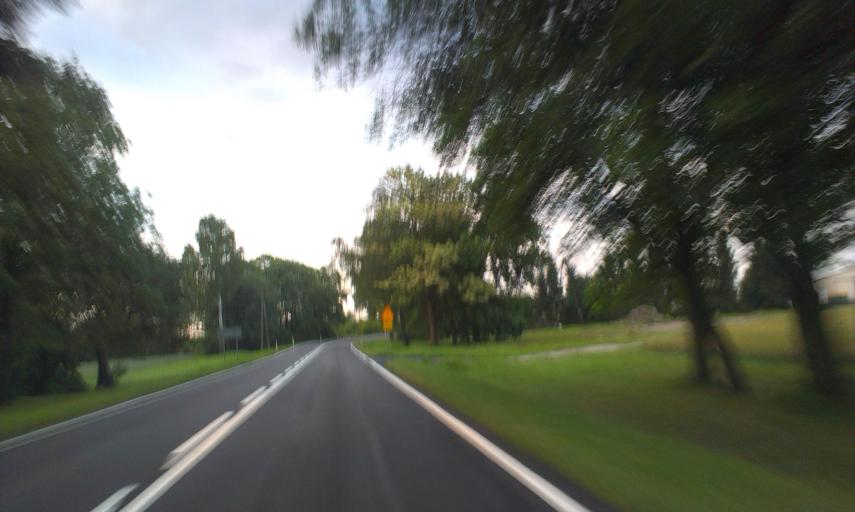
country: PL
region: Greater Poland Voivodeship
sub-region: Powiat zlotowski
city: Okonek
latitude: 53.6088
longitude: 16.7963
